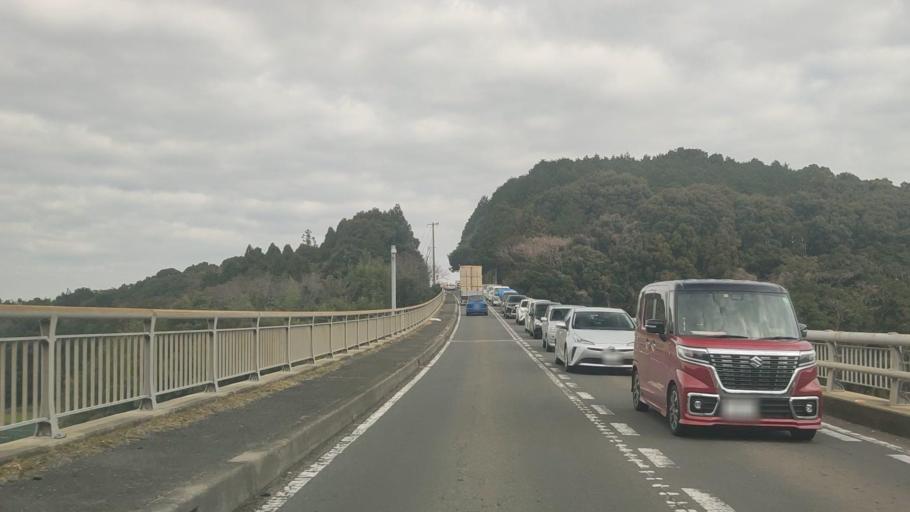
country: JP
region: Nagasaki
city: Shimabara
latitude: 32.8370
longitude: 130.2136
